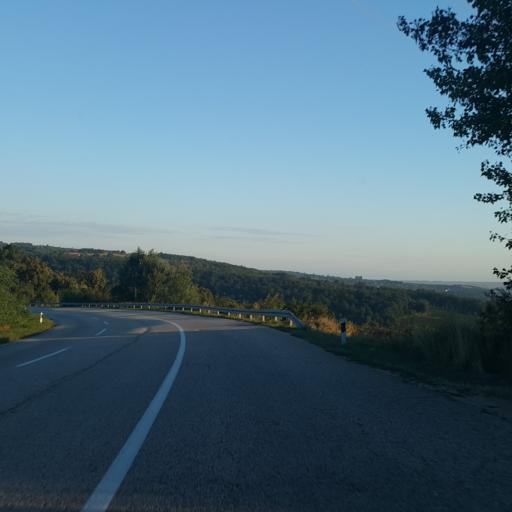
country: RS
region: Central Serbia
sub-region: Borski Okrug
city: Negotin
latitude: 44.2128
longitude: 22.4939
